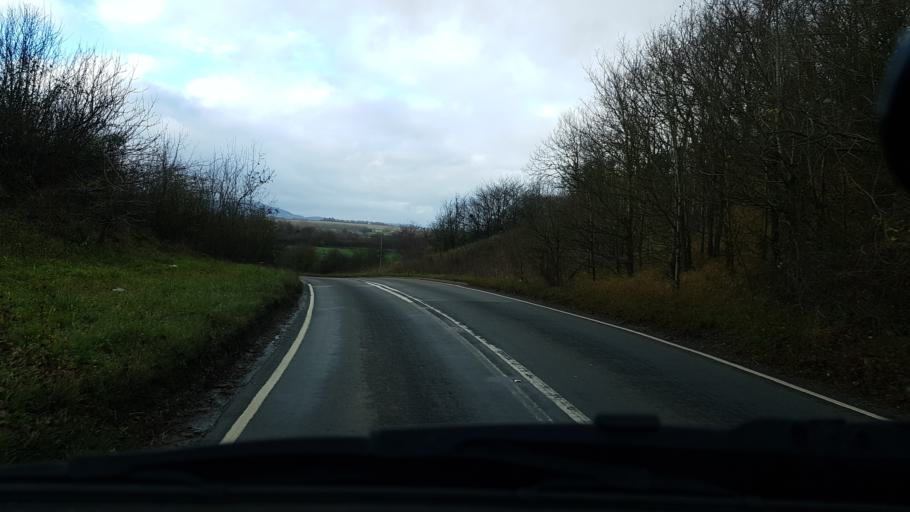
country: GB
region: England
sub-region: Worcestershire
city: Upton upon Severn
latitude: 52.0761
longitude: -2.1612
